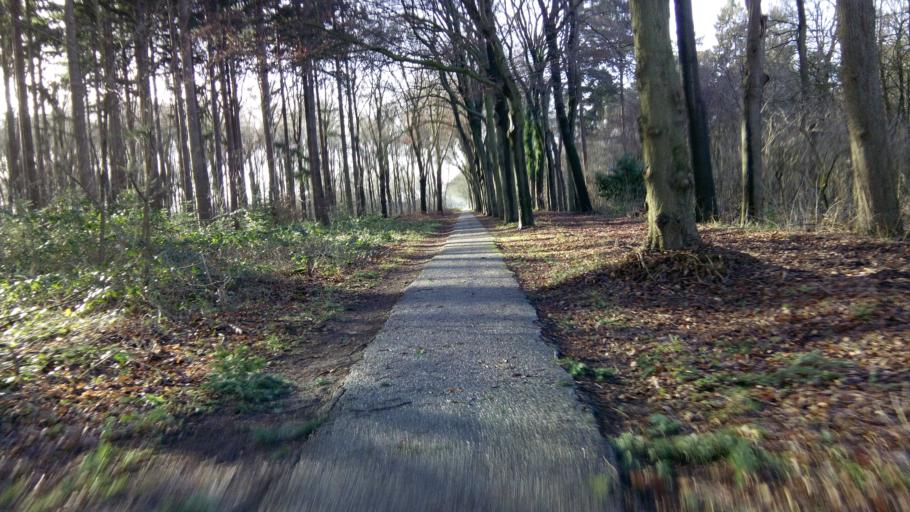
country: NL
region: Gelderland
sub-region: Gemeente Nijmegen
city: Nijmegen
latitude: 51.8008
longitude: 5.8457
